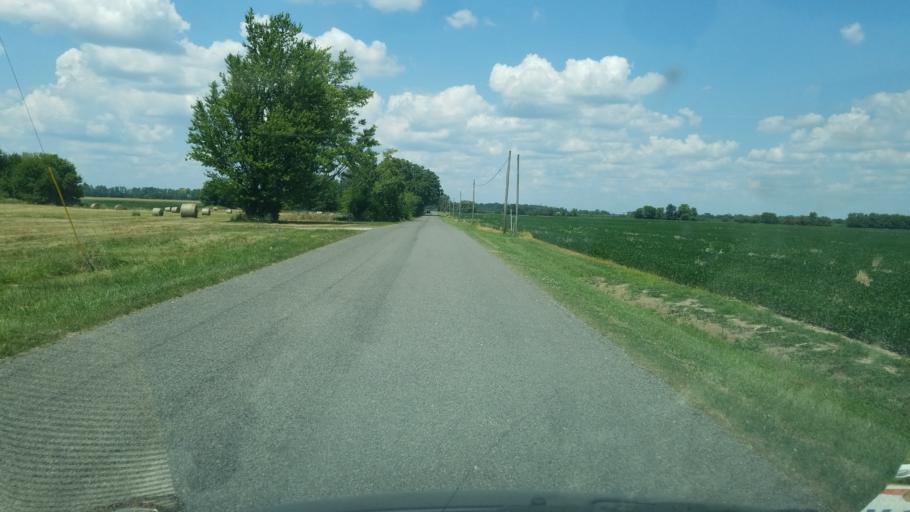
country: US
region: Ohio
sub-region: Champaign County
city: Mechanicsburg
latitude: 40.1013
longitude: -83.4681
